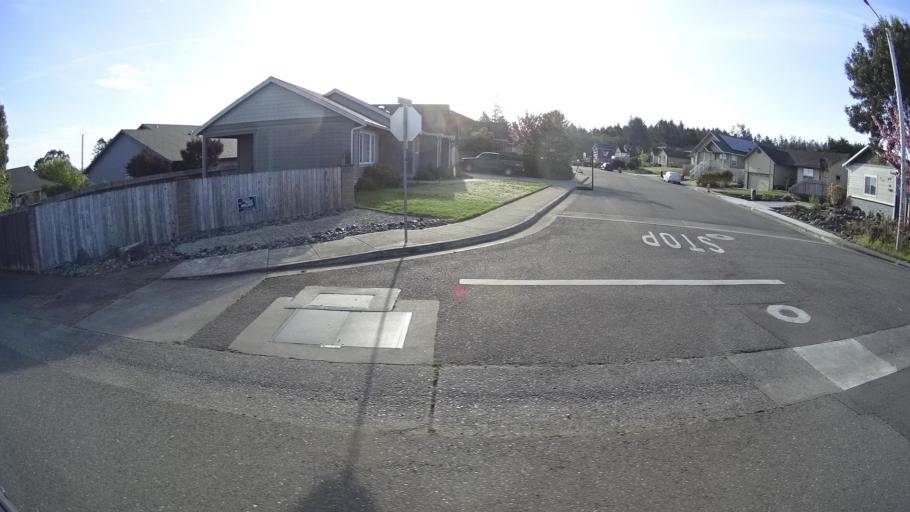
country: US
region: California
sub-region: Humboldt County
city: Humboldt Hill
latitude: 40.7325
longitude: -124.2021
